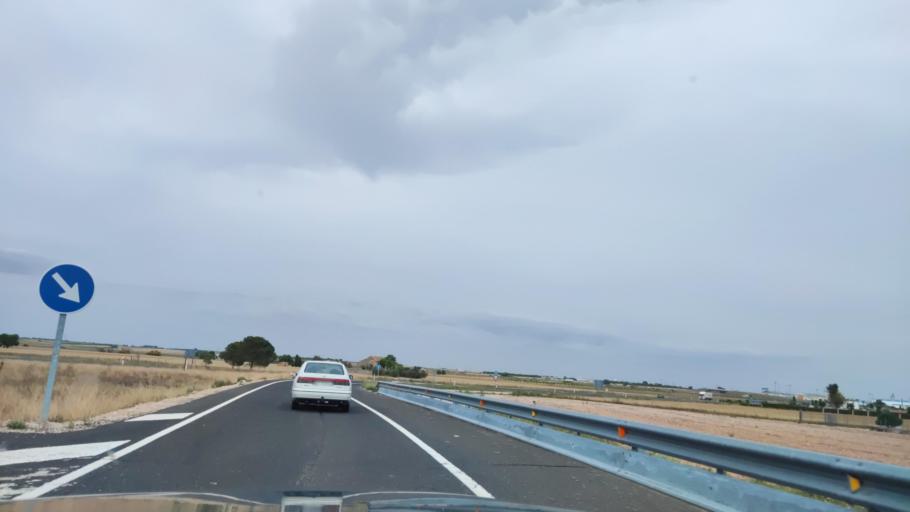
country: ES
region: Castille-La Mancha
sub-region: Provincia de Albacete
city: La Roda
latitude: 39.2190
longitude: -2.1902
